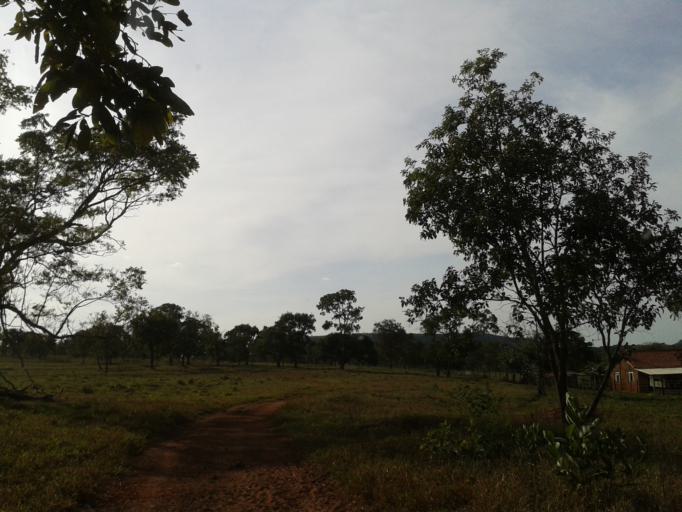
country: BR
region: Minas Gerais
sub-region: Campina Verde
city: Campina Verde
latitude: -19.5210
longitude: -49.6114
